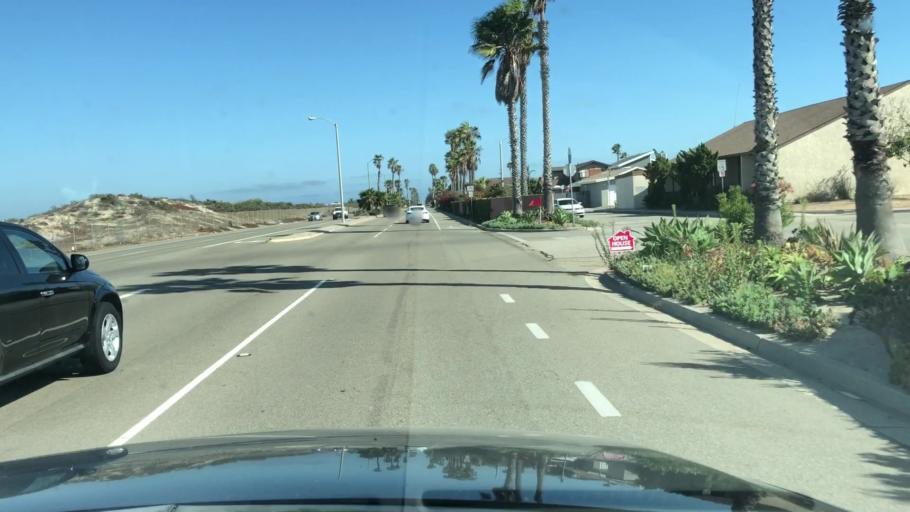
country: US
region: California
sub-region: Ventura County
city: Oxnard Shores
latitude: 34.1883
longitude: -119.2374
